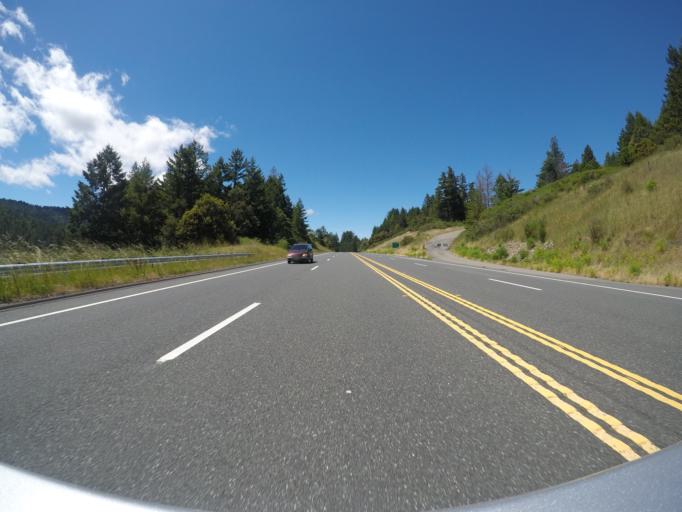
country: US
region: California
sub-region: Humboldt County
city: Redway
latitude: 39.9371
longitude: -123.7738
